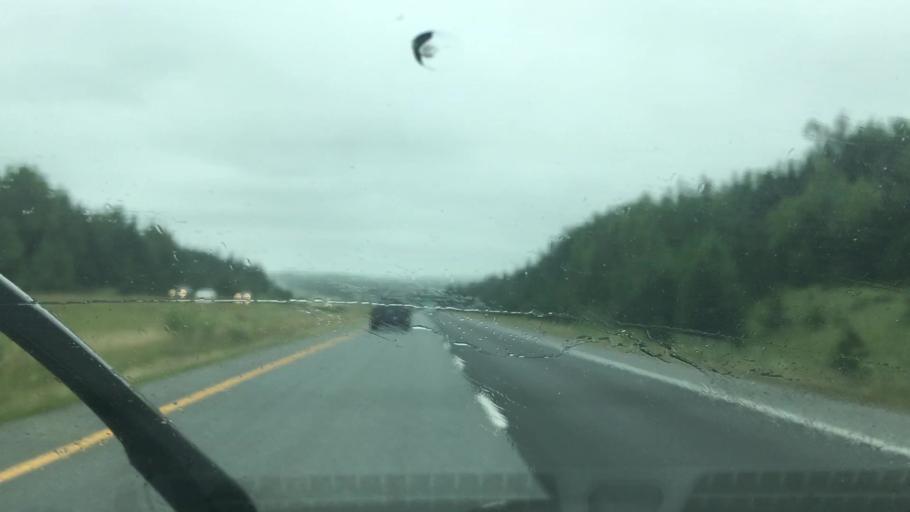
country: CA
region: Nova Scotia
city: Truro
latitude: 45.2419
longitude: -63.2929
